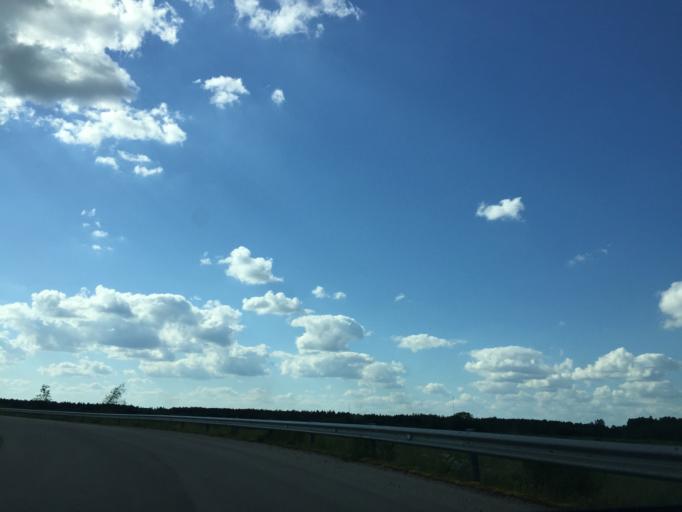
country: LV
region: Jaunpils
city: Jaunpils
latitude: 56.8557
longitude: 23.0222
